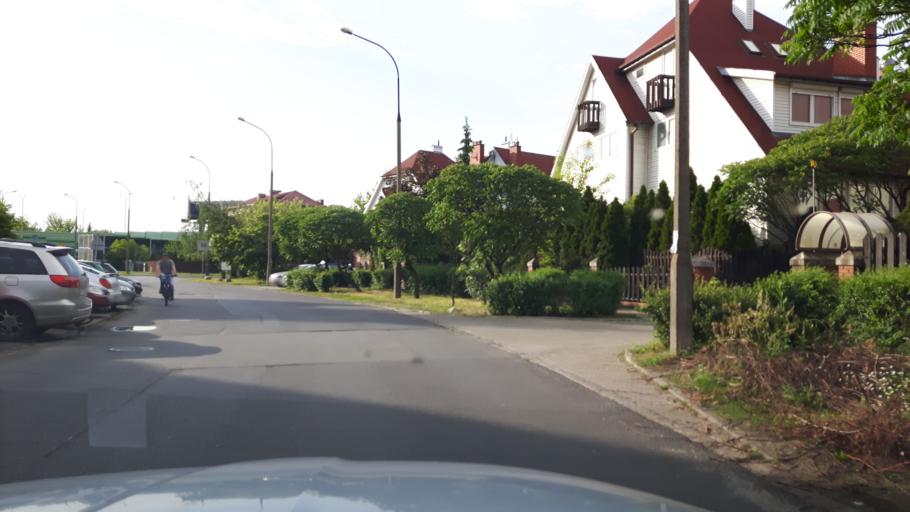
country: PL
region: Masovian Voivodeship
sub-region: Warszawa
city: Rembertow
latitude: 52.2365
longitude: 21.1327
